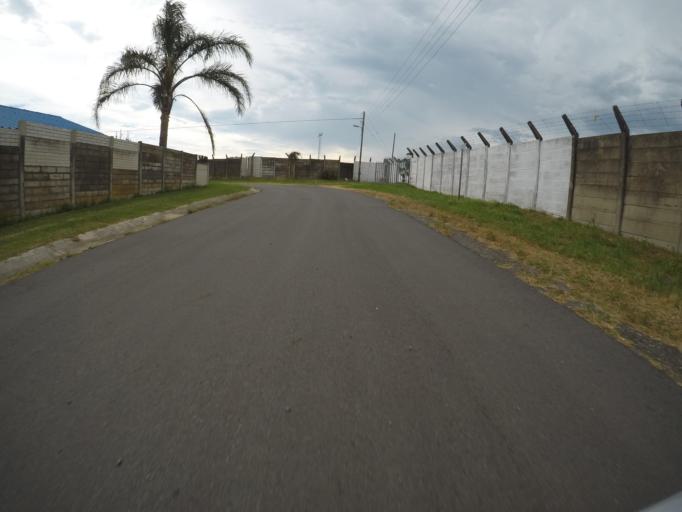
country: ZA
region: Eastern Cape
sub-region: Buffalo City Metropolitan Municipality
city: East London
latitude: -33.0229
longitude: 27.8633
